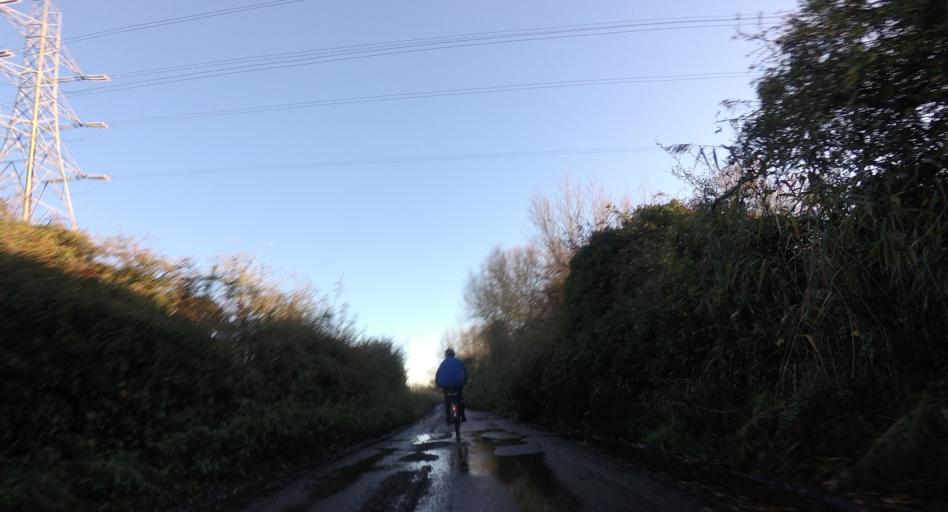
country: GB
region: England
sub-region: West Sussex
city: Steyning
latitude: 50.8949
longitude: -0.3140
